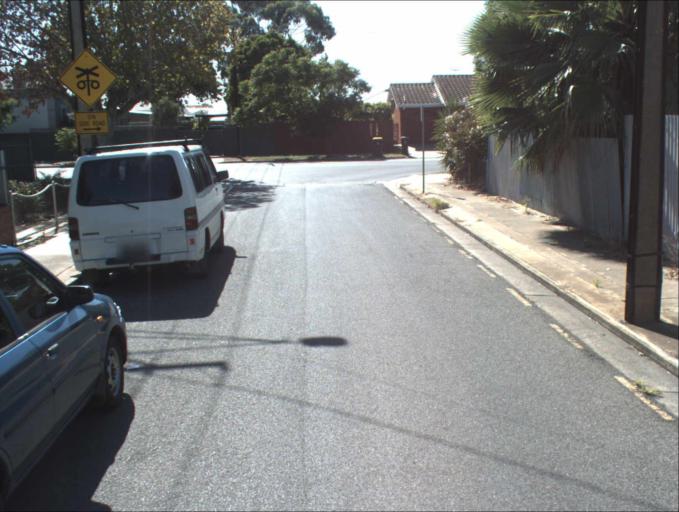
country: AU
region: South Australia
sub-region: Port Adelaide Enfield
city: Alberton
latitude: -34.8526
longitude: 138.5209
